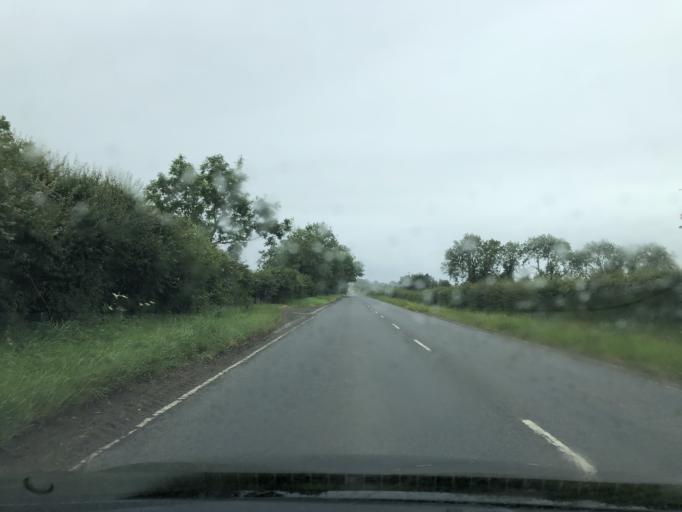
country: GB
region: Northern Ireland
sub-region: Down District
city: Dundrum
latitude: 54.3012
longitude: -5.8400
